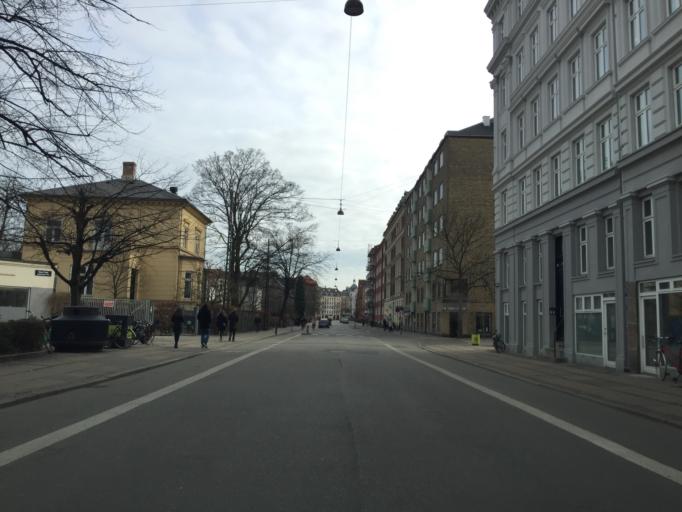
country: DK
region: Capital Region
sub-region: Kobenhavn
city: Copenhagen
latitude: 55.7052
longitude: 12.5807
